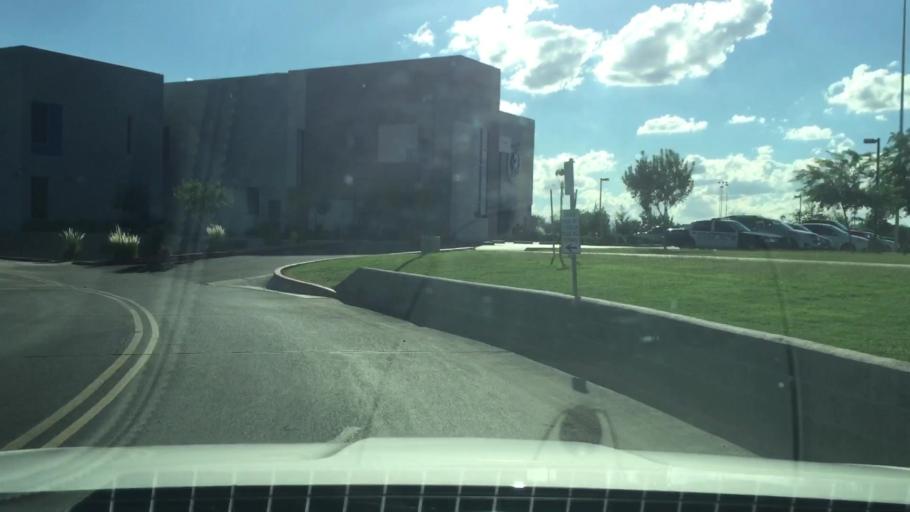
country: US
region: Arizona
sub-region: Maricopa County
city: San Carlos
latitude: 33.3639
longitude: -111.8676
